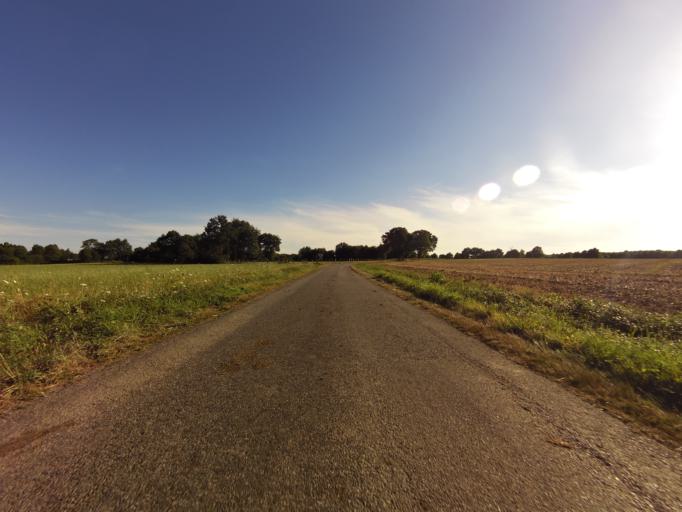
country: FR
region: Brittany
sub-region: Departement du Morbihan
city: Pluherlin
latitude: 47.7288
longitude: -2.3475
